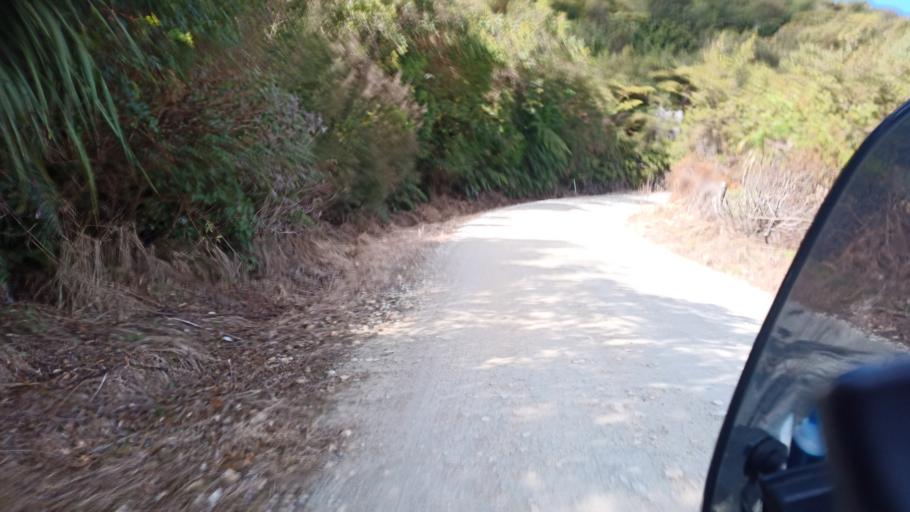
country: NZ
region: Gisborne
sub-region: Gisborne District
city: Gisborne
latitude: -38.8529
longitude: 177.7909
